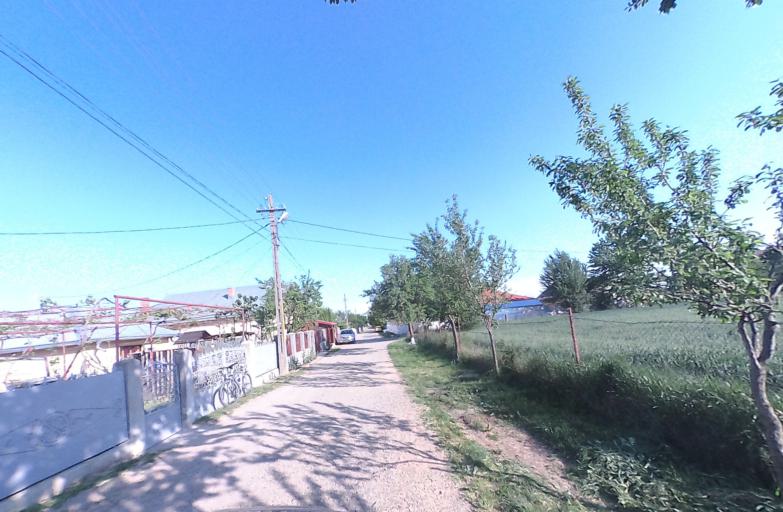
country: RO
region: Neamt
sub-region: Comuna Cordun
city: Pildesti
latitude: 46.9823
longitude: 26.8046
